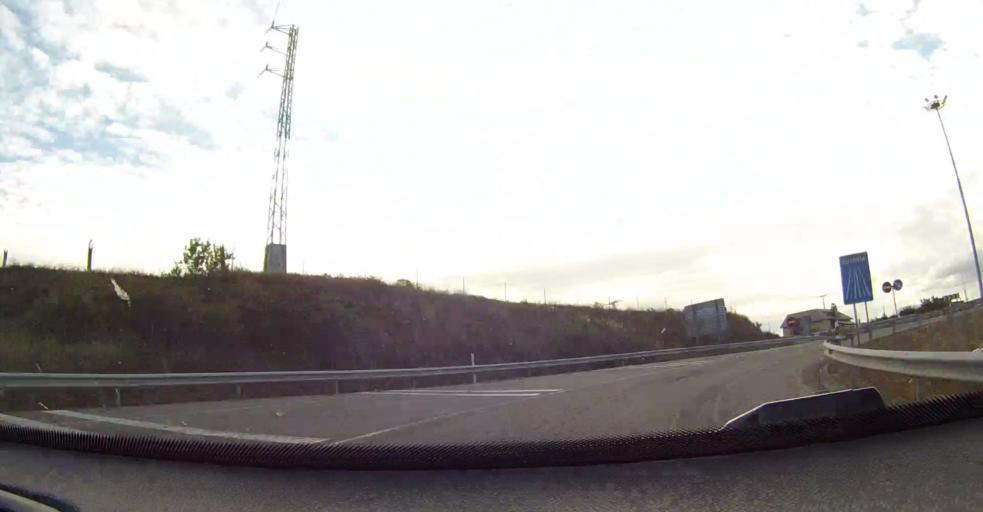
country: ES
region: Castille and Leon
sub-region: Provincia de Leon
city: Leon
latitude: 42.5683
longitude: -5.5829
